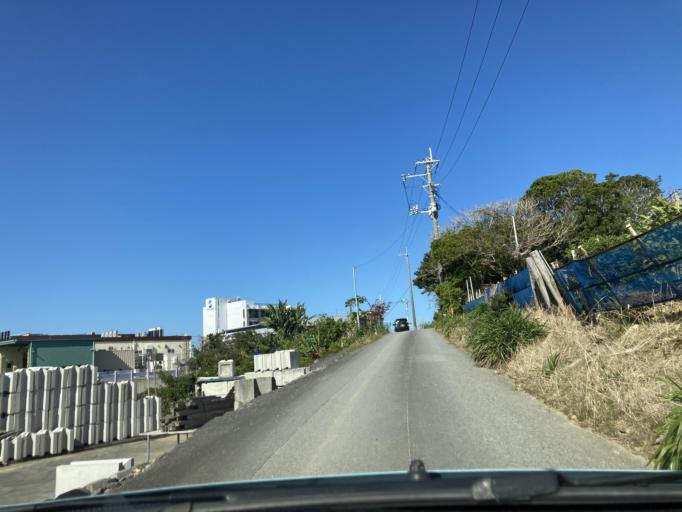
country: JP
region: Okinawa
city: Okinawa
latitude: 26.3679
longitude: 127.8271
